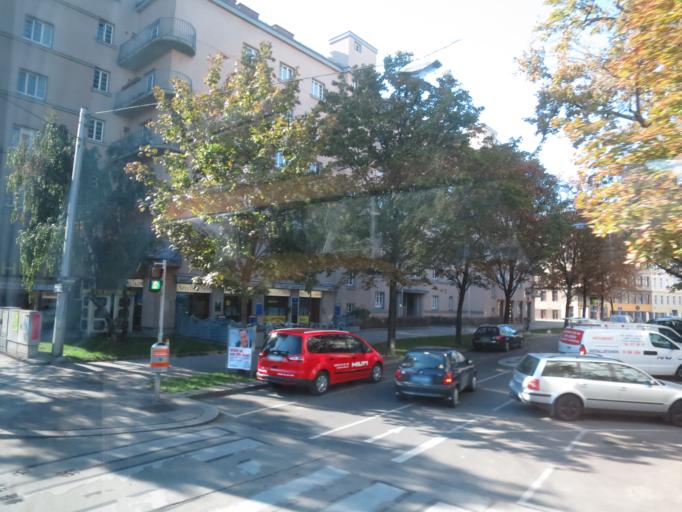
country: AT
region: Vienna
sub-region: Wien Stadt
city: Vienna
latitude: 48.1856
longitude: 16.3441
